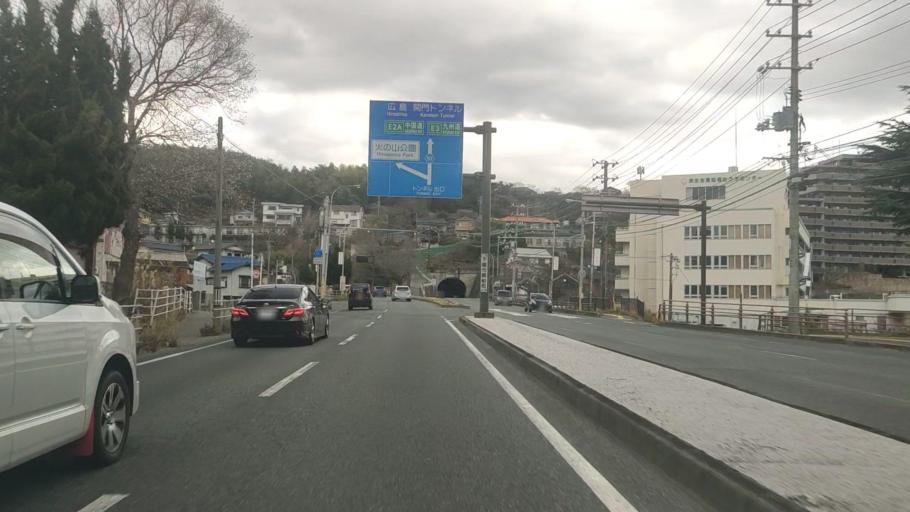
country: JP
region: Yamaguchi
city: Shimonoseki
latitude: 33.9690
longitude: 130.9415
